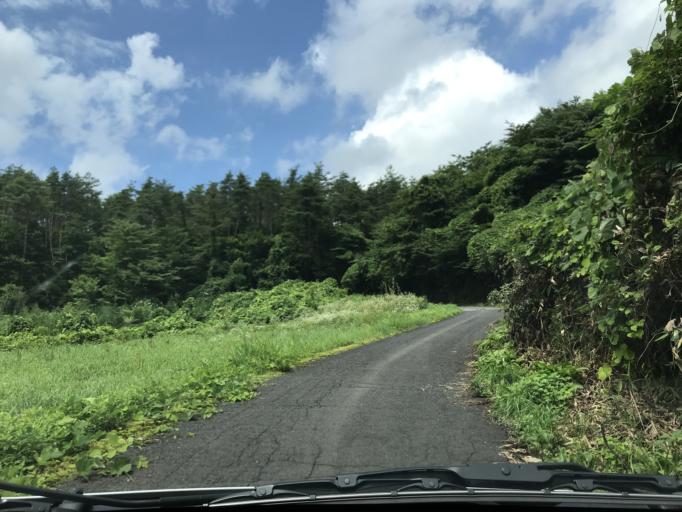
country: JP
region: Iwate
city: Mizusawa
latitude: 39.0576
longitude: 141.3816
